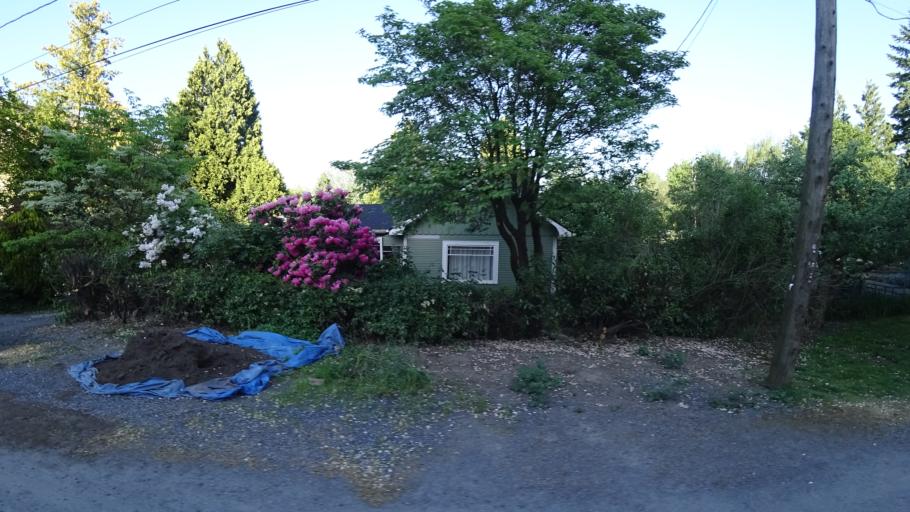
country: US
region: Oregon
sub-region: Multnomah County
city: Portland
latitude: 45.5568
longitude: -122.6862
